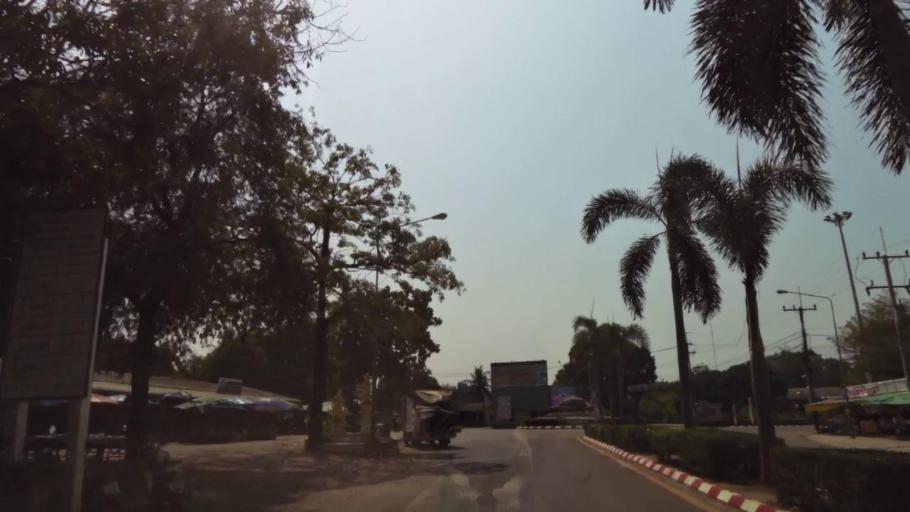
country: TH
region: Chanthaburi
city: Tha Mai
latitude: 12.5623
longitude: 101.9132
